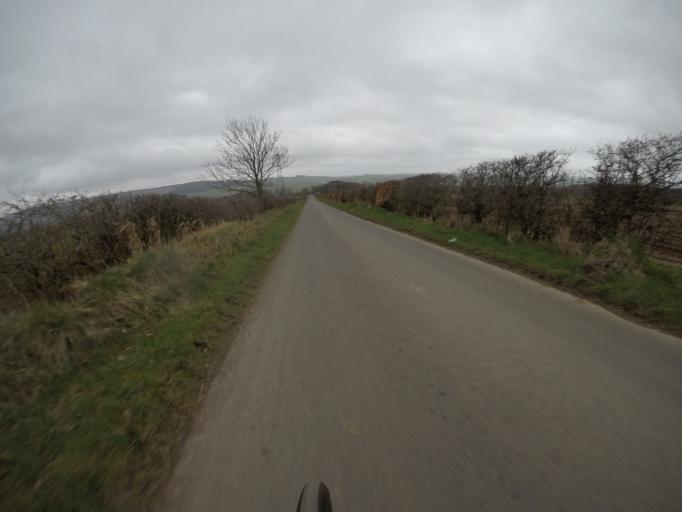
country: GB
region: Scotland
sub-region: East Ayrshire
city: Newmilns
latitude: 55.6200
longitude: -4.3433
